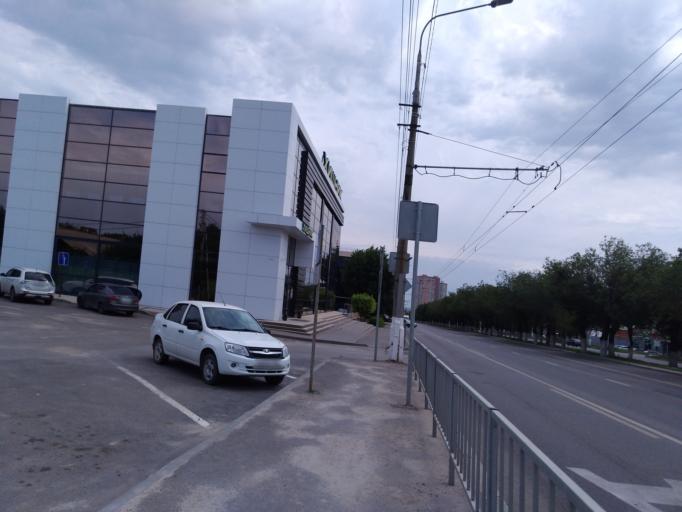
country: RU
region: Volgograd
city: Volgograd
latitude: 48.7287
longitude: 44.4990
